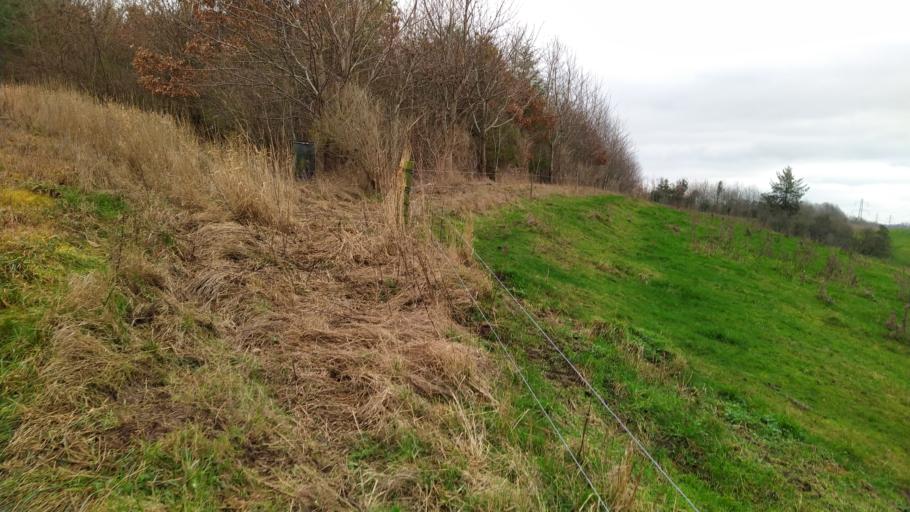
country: DK
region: Capital Region
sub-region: Egedal Kommune
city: Stenlose
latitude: 55.7575
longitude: 12.2151
